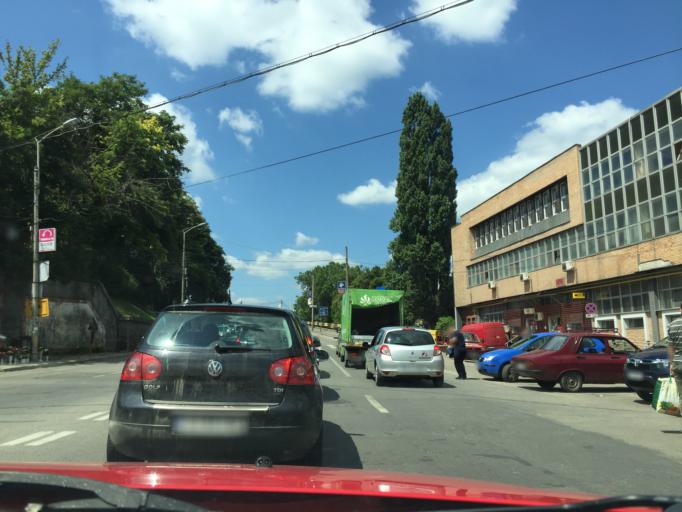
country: RO
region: Cluj
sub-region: Municipiul Cluj-Napoca
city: Cluj-Napoca
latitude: 46.7840
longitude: 23.5857
